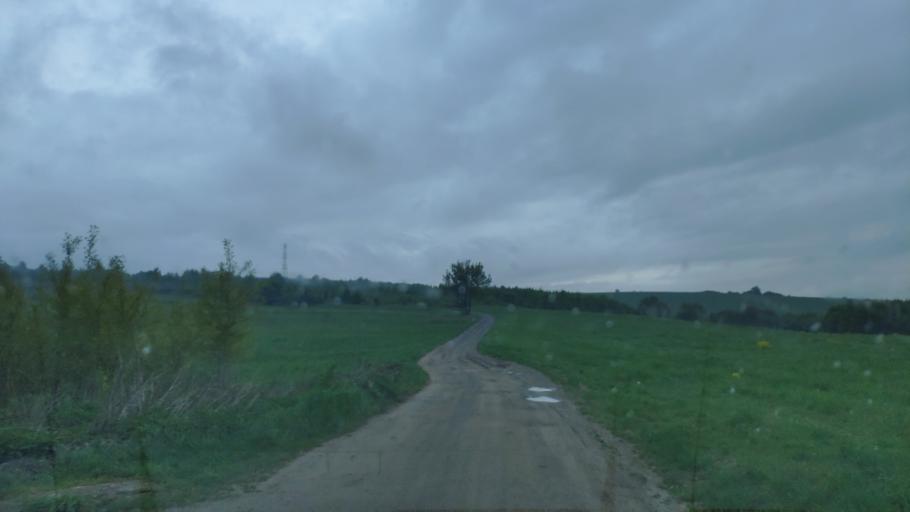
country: SK
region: Kosicky
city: Kosice
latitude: 48.7603
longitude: 21.2002
